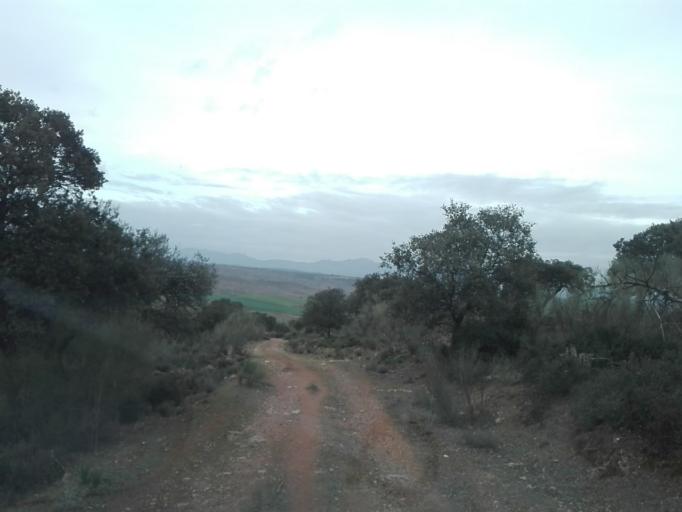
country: ES
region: Extremadura
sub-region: Provincia de Badajoz
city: Hinojosa del Valle
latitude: 38.4399
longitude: -6.1895
